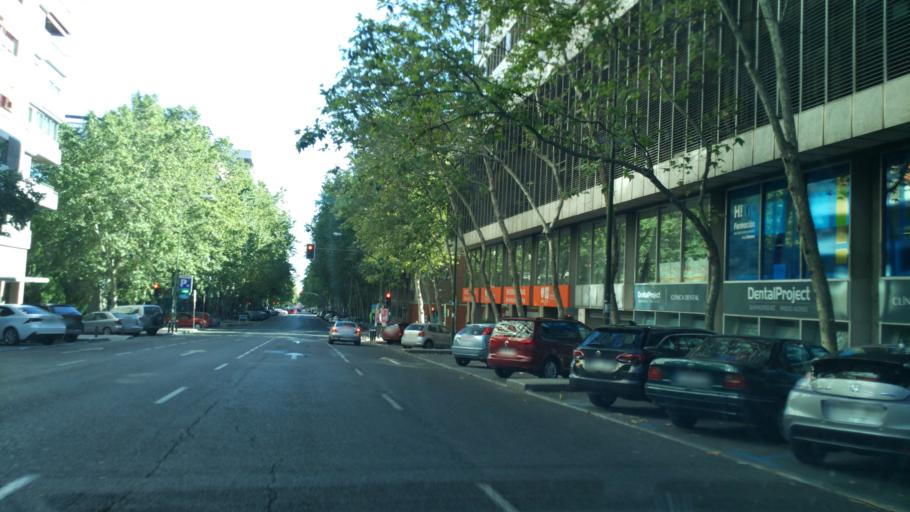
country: ES
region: Madrid
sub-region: Provincia de Madrid
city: Chamartin
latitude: 40.4584
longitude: -3.6944
